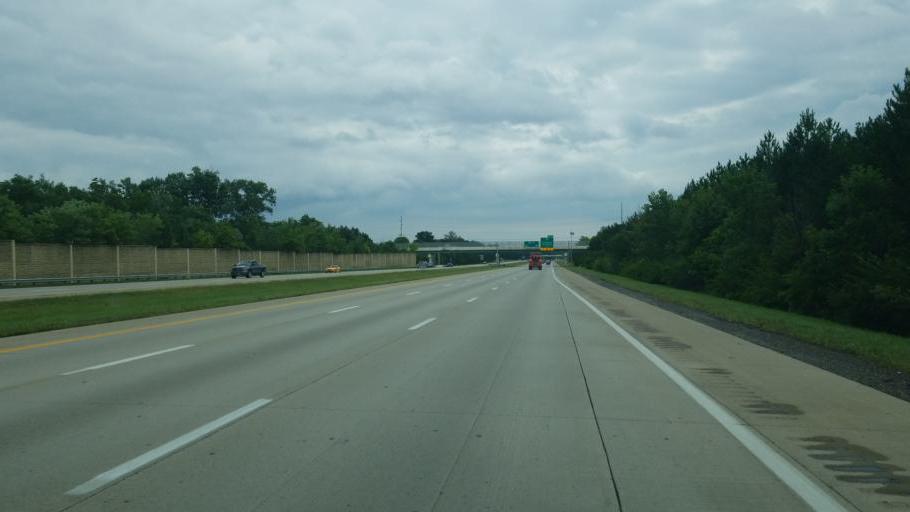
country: US
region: Ohio
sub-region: Franklin County
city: Grove City
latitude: 39.9022
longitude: -83.0676
